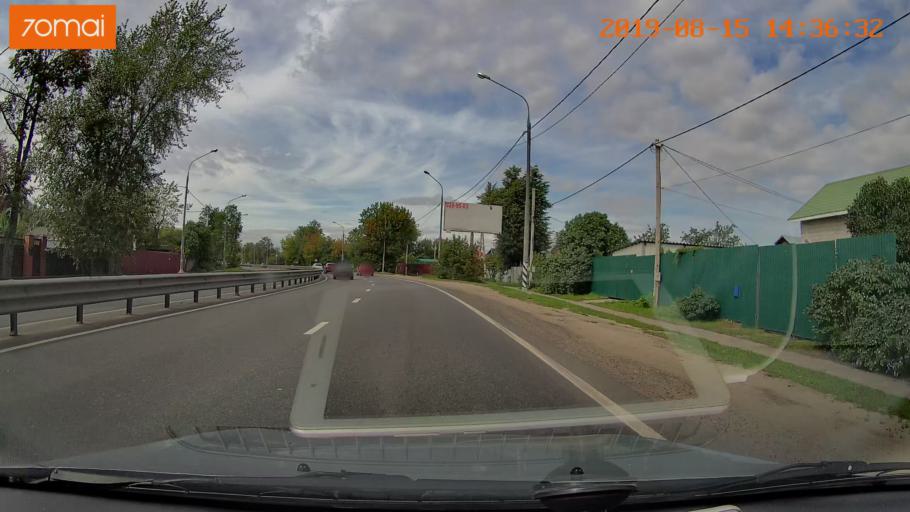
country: RU
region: Moskovskaya
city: Tomilino
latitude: 55.6471
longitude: 37.9348
